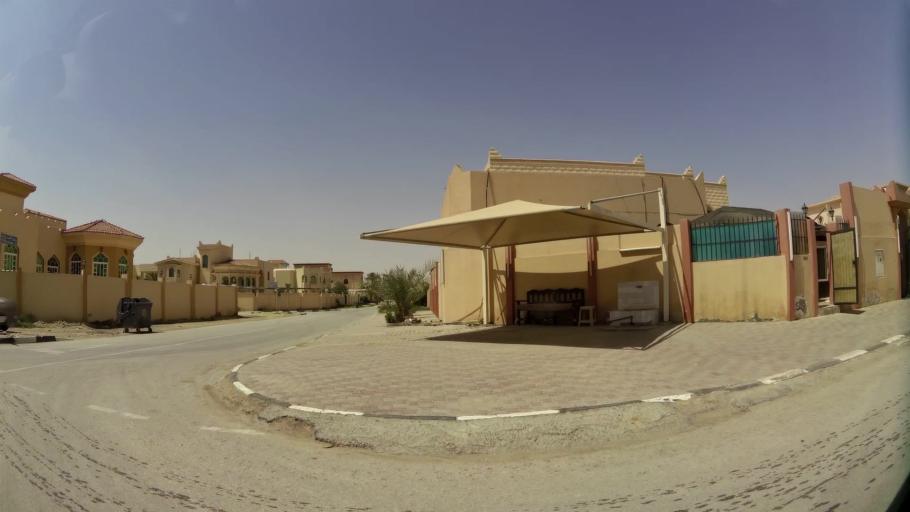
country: QA
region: Baladiyat ar Rayyan
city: Ar Rayyan
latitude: 25.3628
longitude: 51.4784
